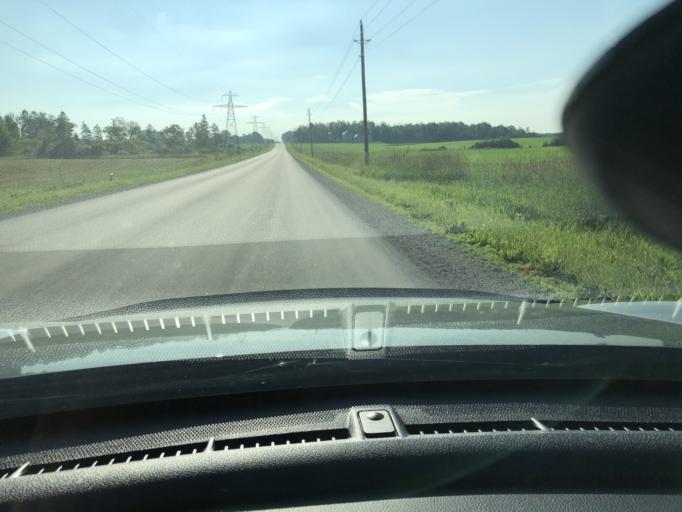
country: CA
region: Ontario
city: Stratford
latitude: 43.3881
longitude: -80.8593
